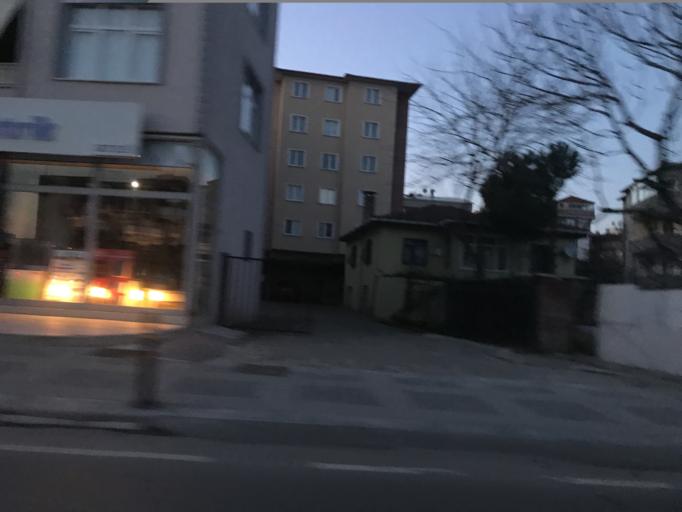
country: TR
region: Istanbul
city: Pendik
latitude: 40.9061
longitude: 29.2872
